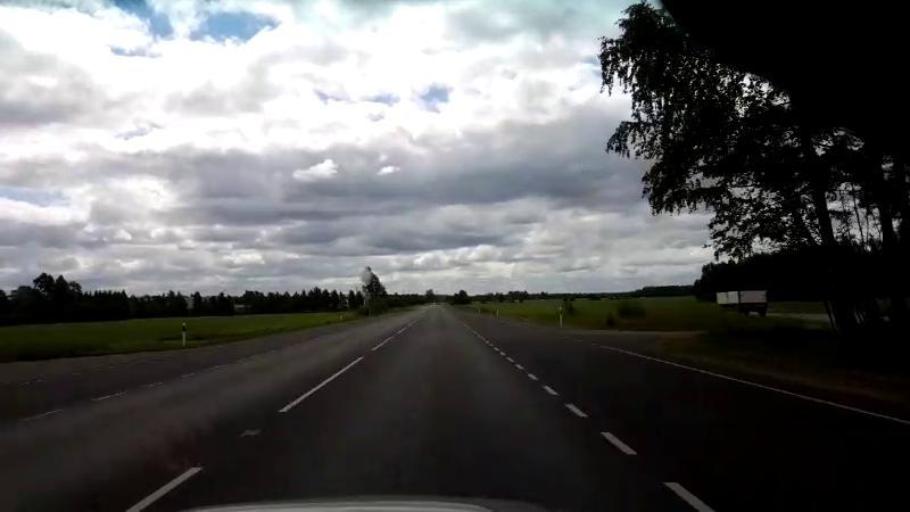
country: EE
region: Paernumaa
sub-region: Paikuse vald
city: Paikuse
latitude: 58.3136
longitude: 24.6035
